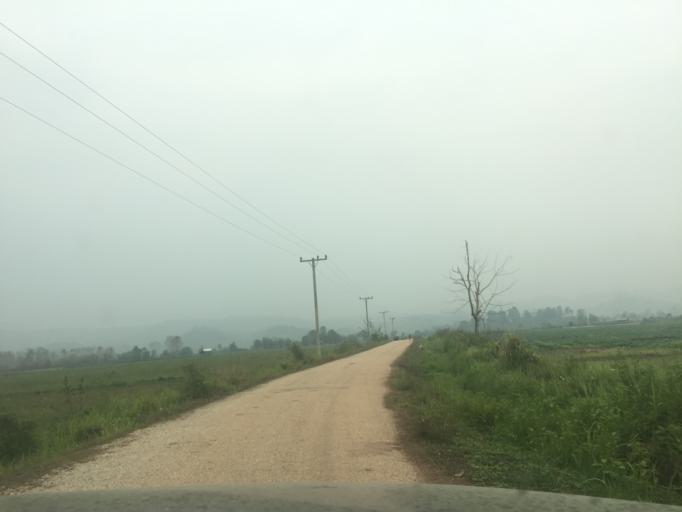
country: LA
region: Xiagnabouli
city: Sainyabuli
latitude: 19.0434
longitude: 101.5150
